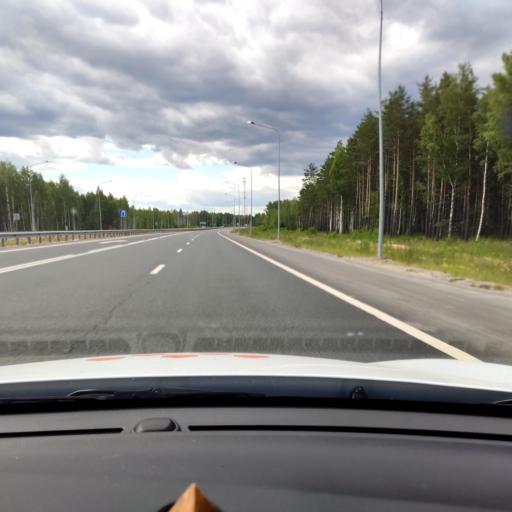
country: RU
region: Mariy-El
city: Surok
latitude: 56.4354
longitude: 48.1196
